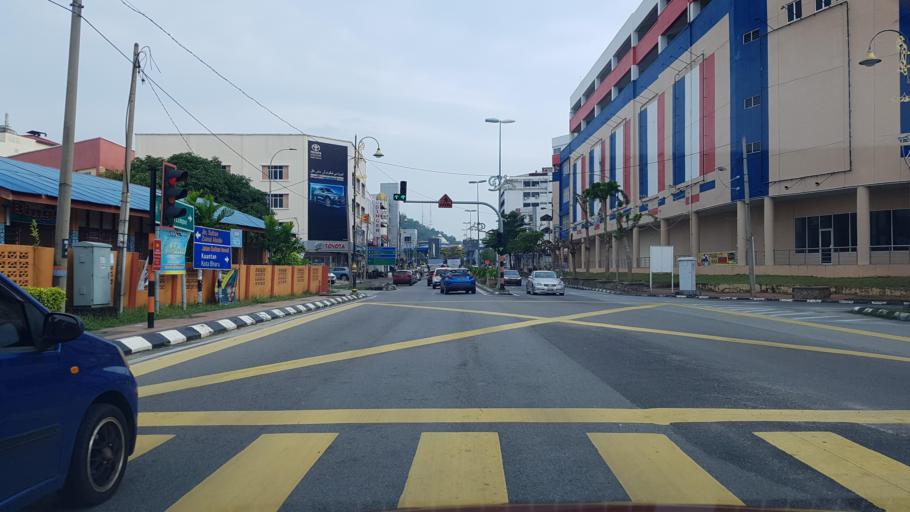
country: MY
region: Terengganu
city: Kuala Terengganu
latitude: 5.3316
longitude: 103.1384
